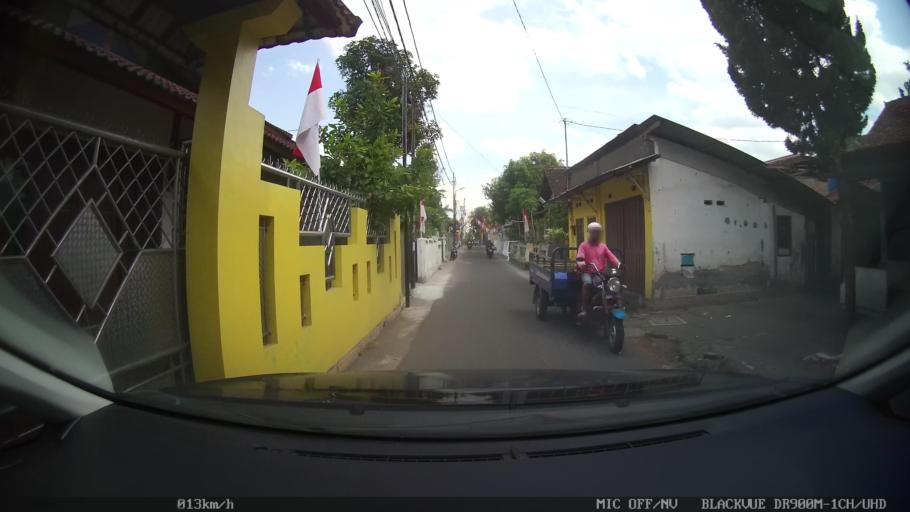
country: ID
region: Daerah Istimewa Yogyakarta
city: Kasihan
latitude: -7.8175
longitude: 110.3545
